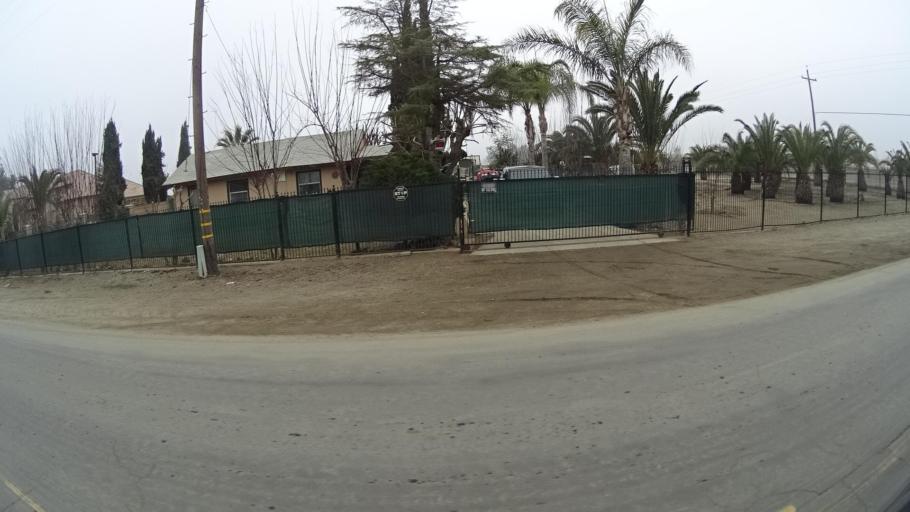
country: US
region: California
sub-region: Kern County
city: Greenfield
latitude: 35.2380
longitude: -119.0740
